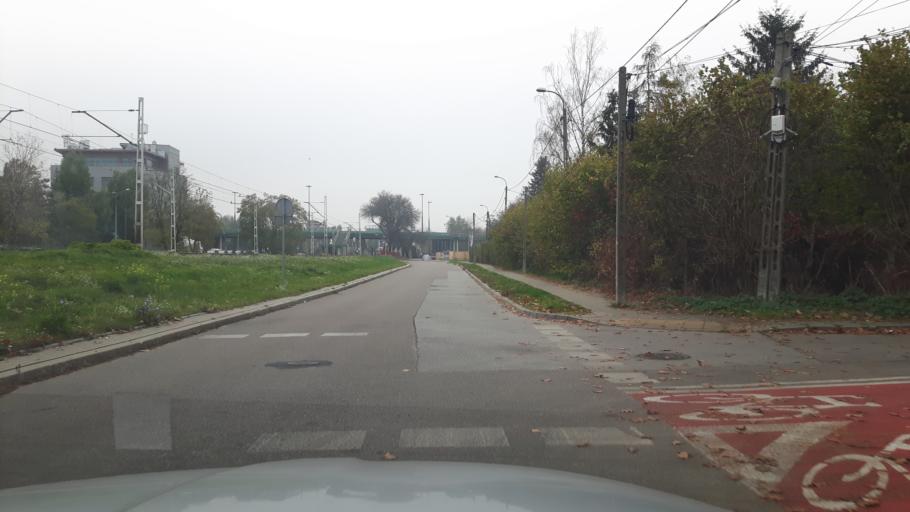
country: PL
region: Masovian Voivodeship
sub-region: Warszawa
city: Wlochy
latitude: 52.1962
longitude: 20.9377
